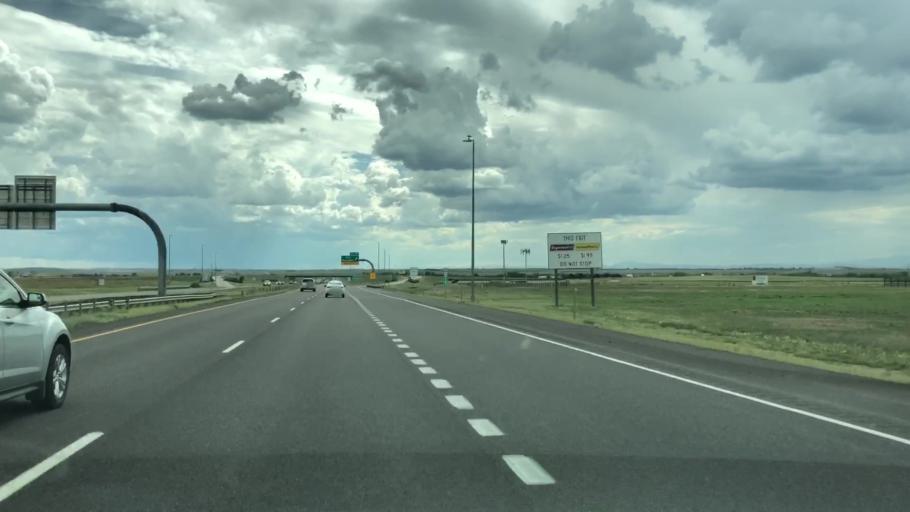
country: US
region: Colorado
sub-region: Adams County
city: Aurora
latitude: 39.7269
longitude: -104.7188
